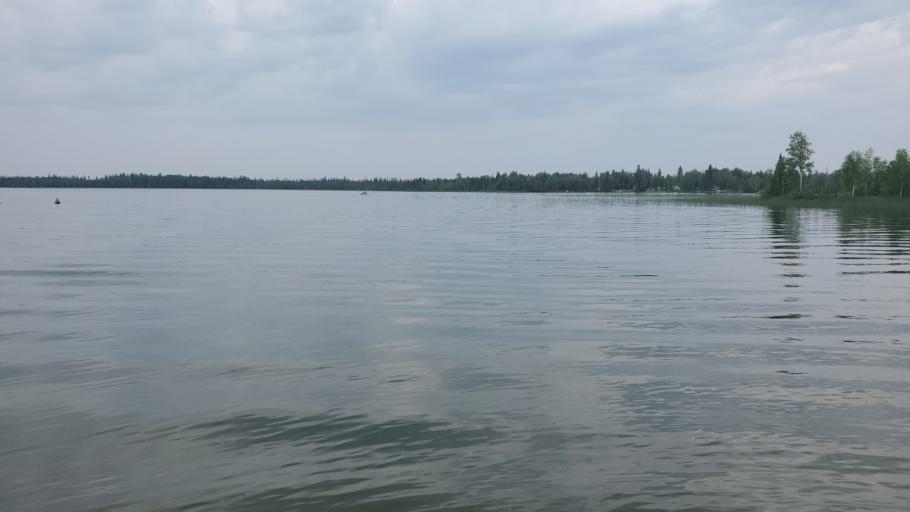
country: CA
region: Ontario
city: Hearst
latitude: 49.6475
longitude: -83.2841
